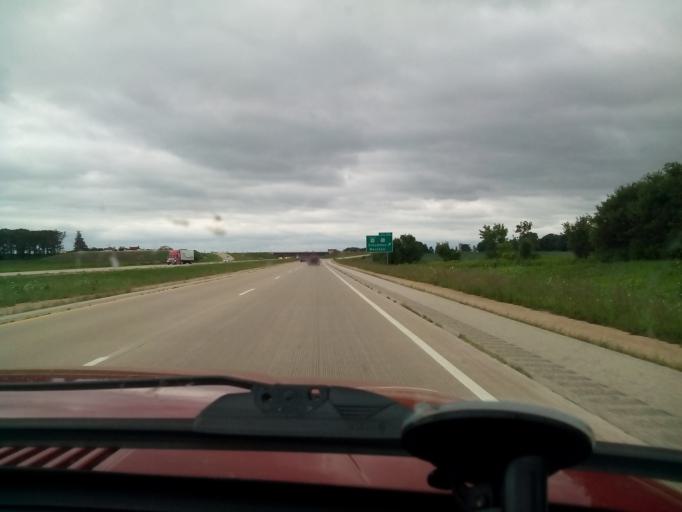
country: US
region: Wisconsin
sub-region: Columbia County
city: Columbus
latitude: 43.3245
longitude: -89.0453
